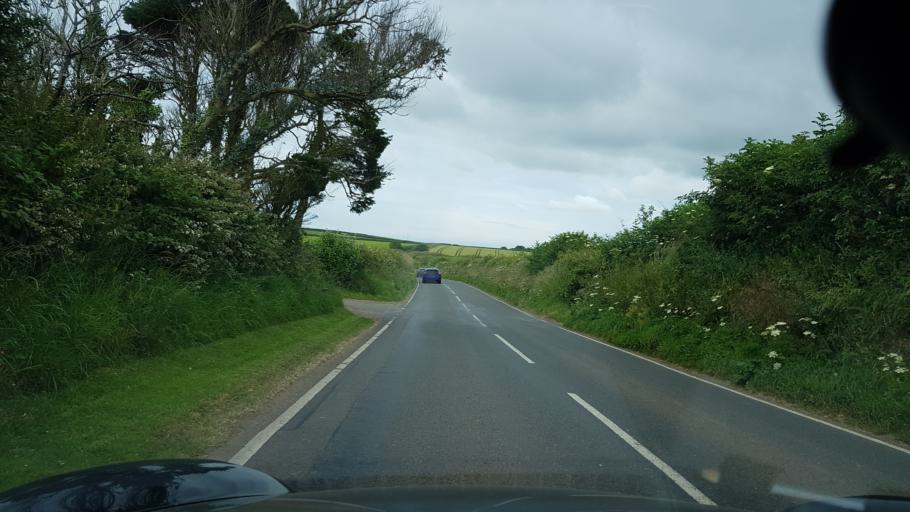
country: GB
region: Wales
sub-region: Pembrokeshire
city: Herbrandston
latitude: 51.7560
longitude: -5.1115
